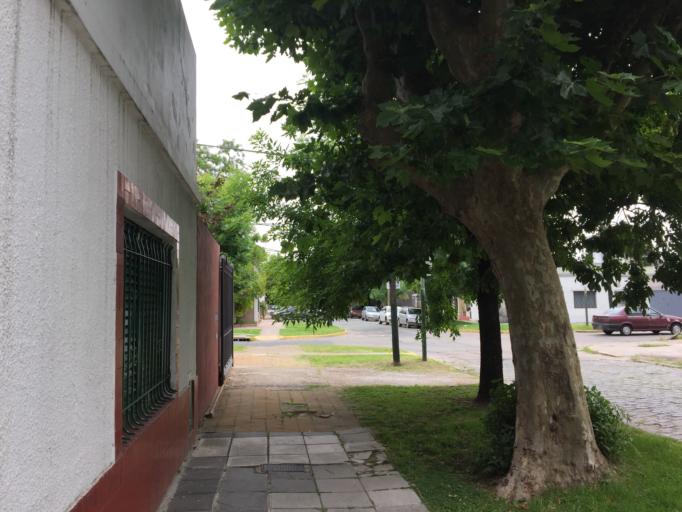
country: AR
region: Buenos Aires
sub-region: Partido de Lomas de Zamora
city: Lomas de Zamora
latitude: -34.7560
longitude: -58.3926
